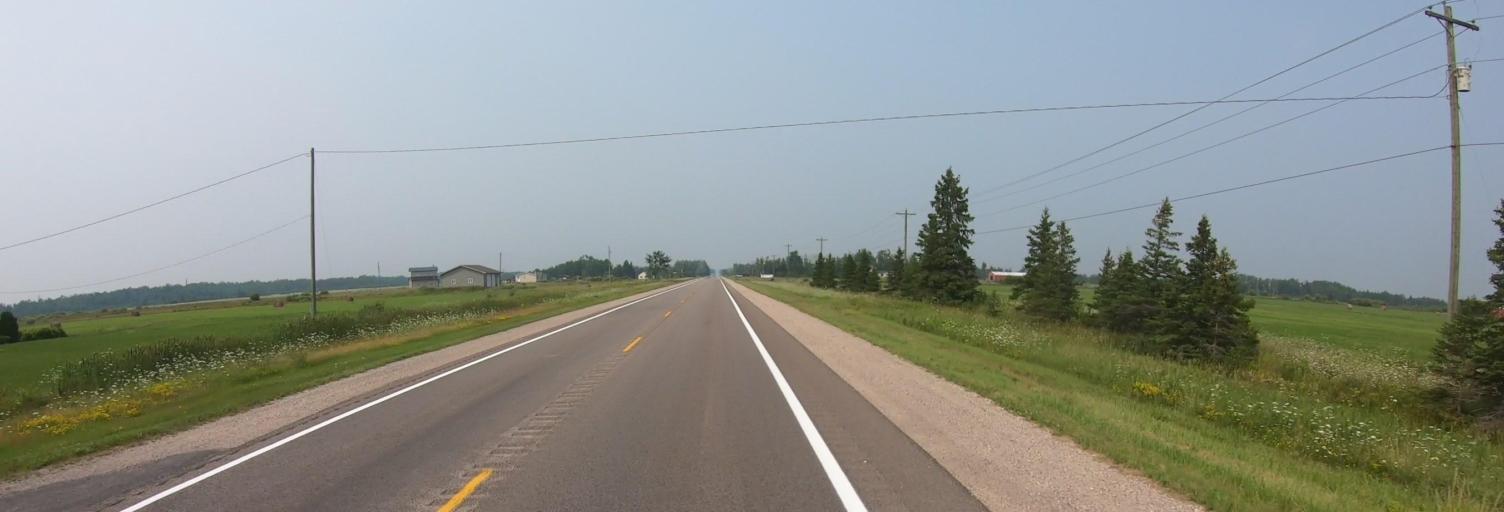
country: US
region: Michigan
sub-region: Chippewa County
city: Sault Ste. Marie
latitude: 46.1704
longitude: -84.3635
